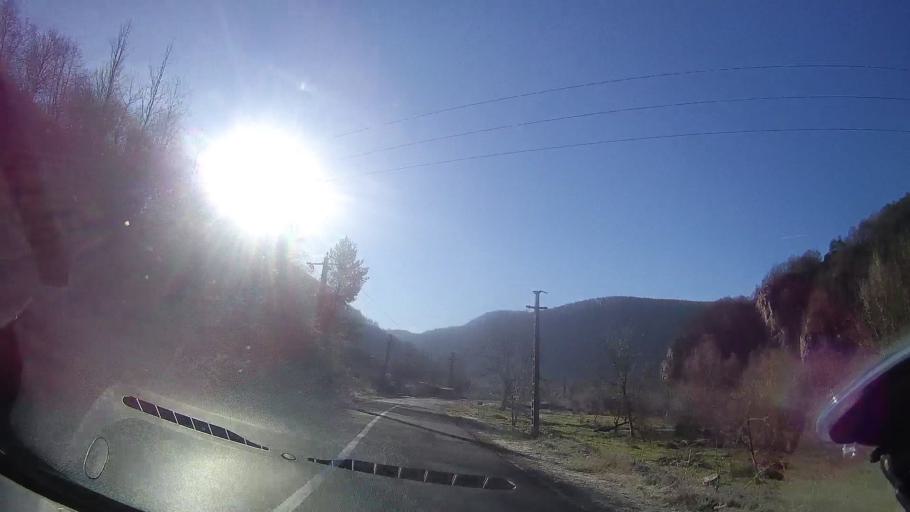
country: RO
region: Bihor
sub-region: Comuna Bulz
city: Bulz
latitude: 46.9287
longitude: 22.6588
